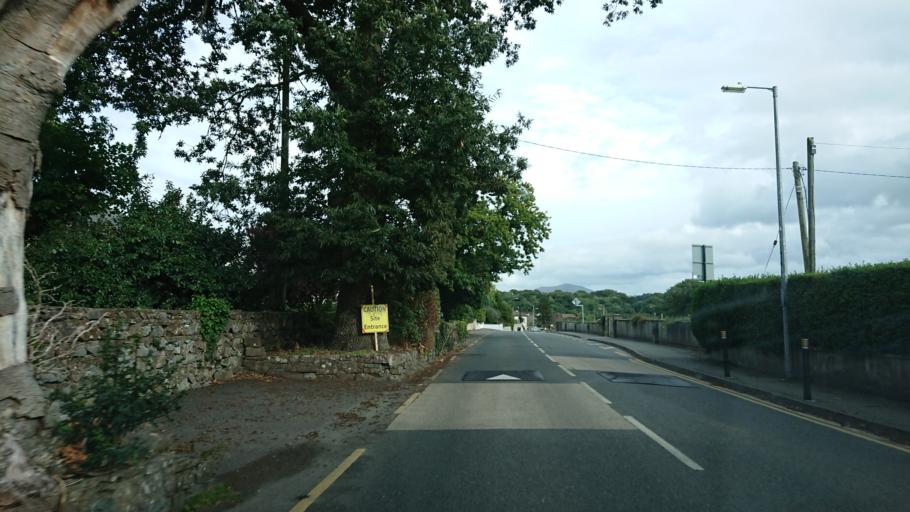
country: IE
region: Munster
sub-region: Ciarrai
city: Cill Airne
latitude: 52.0554
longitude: -9.4911
